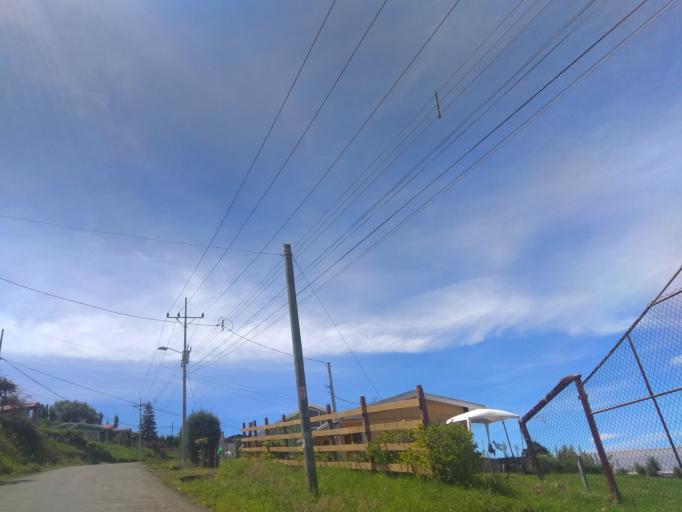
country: CR
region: Cartago
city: Cot
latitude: 9.9174
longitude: -83.8981
